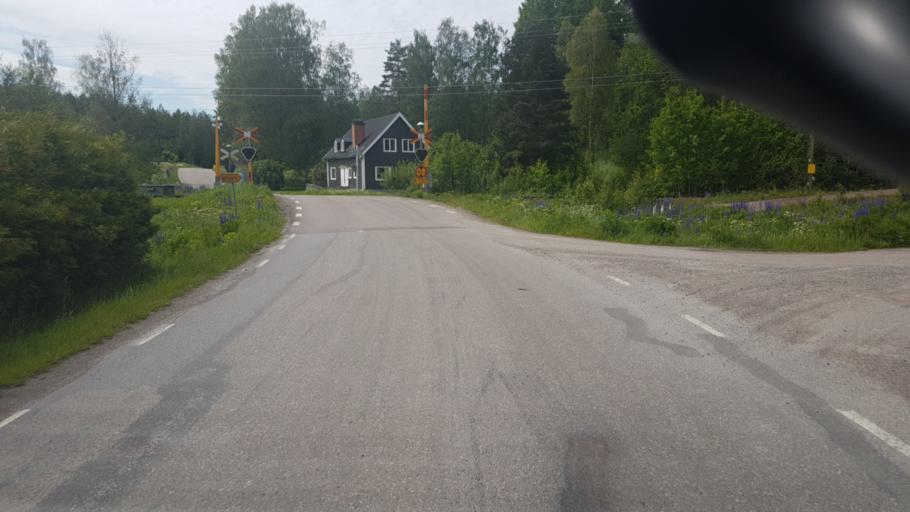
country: SE
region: Vaermland
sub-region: Eda Kommun
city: Charlottenberg
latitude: 59.8574
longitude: 12.3438
